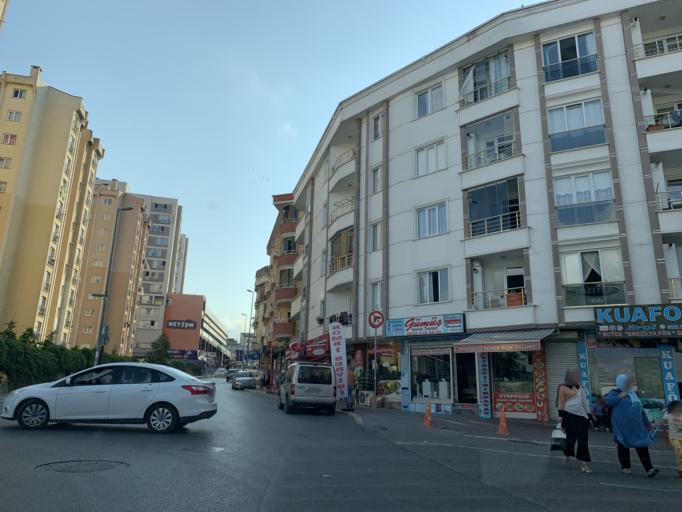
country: TR
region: Istanbul
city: Esenyurt
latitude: 41.0428
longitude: 28.6796
